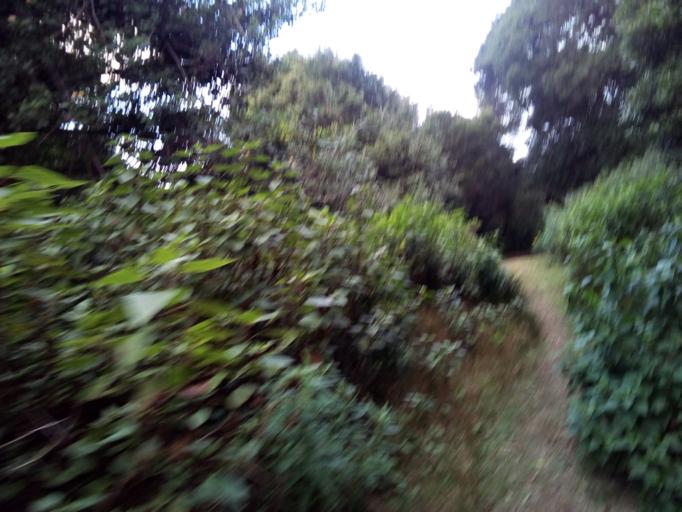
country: AU
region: New South Wales
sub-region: Wollongong
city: Keiraville
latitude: -34.4050
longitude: 150.8612
